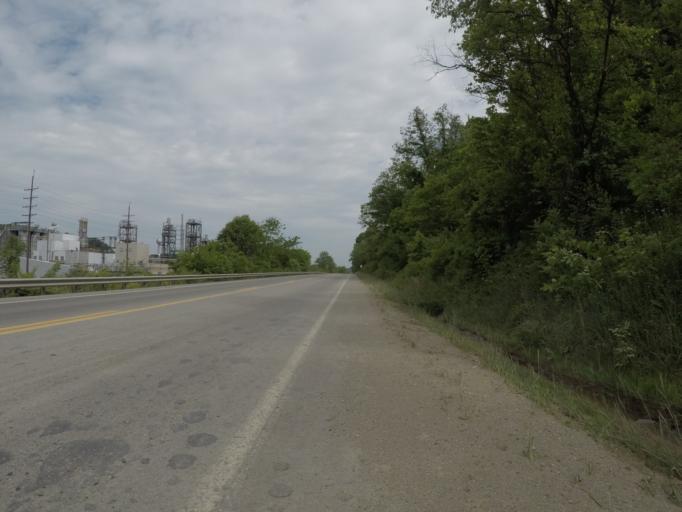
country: US
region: West Virginia
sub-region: Wayne County
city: Kenova
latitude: 38.3526
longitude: -82.5933
